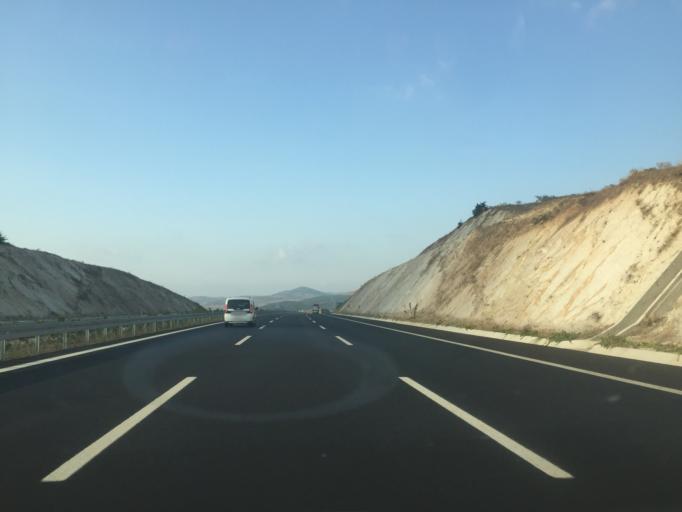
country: TR
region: Balikesir
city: Ertugrul
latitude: 39.6223
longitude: 27.7033
